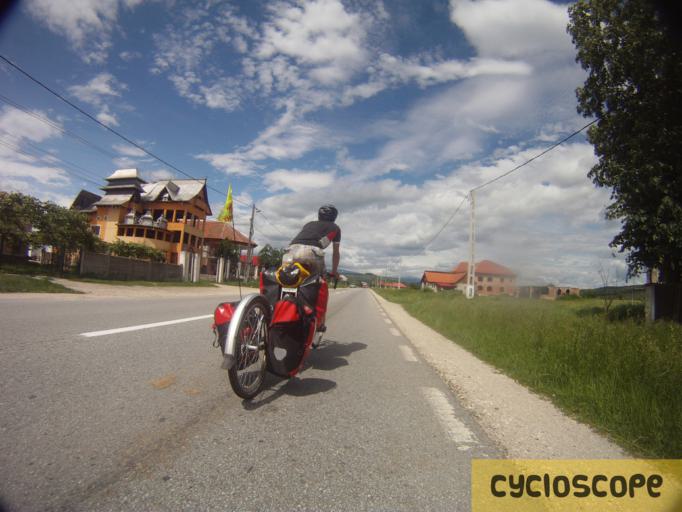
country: RO
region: Gorj
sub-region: Comuna Baia de Fier
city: Baia de Fier
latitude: 45.1383
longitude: 23.7359
